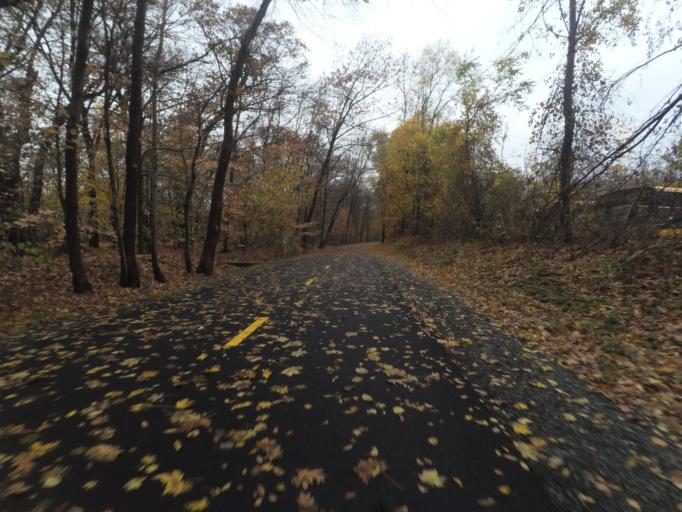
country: US
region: Massachusetts
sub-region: Middlesex County
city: Lexington
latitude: 42.4627
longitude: -71.2424
